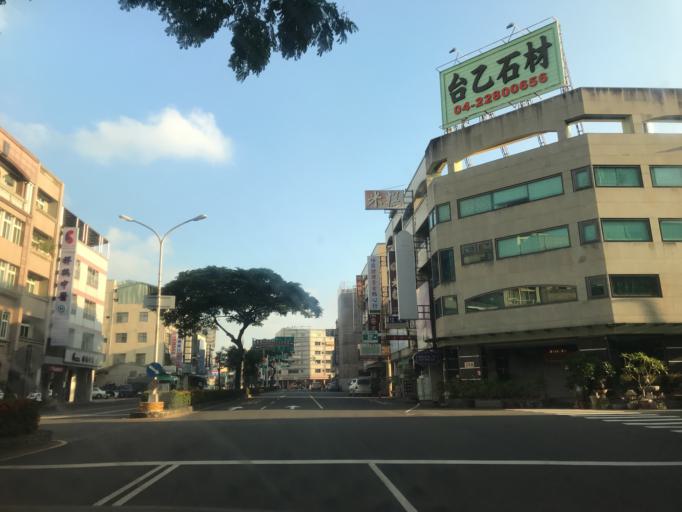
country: TW
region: Taiwan
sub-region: Taichung City
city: Taichung
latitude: 24.1299
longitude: 120.6904
